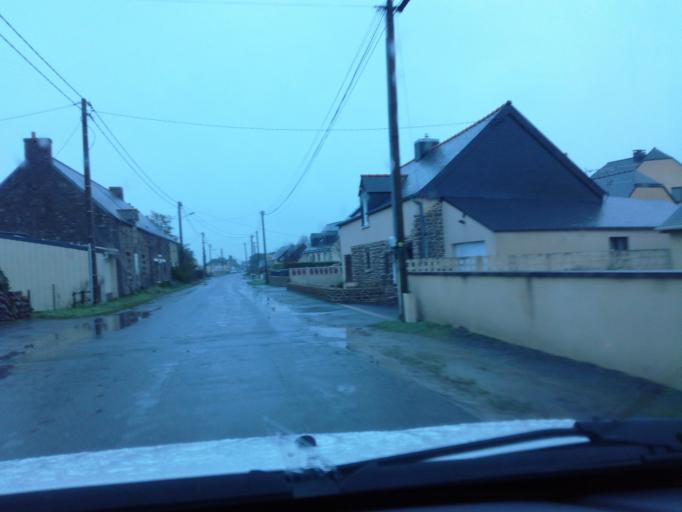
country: FR
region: Brittany
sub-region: Departement d'Ille-et-Vilaine
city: Cherrueix
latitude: 48.6093
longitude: -1.6844
